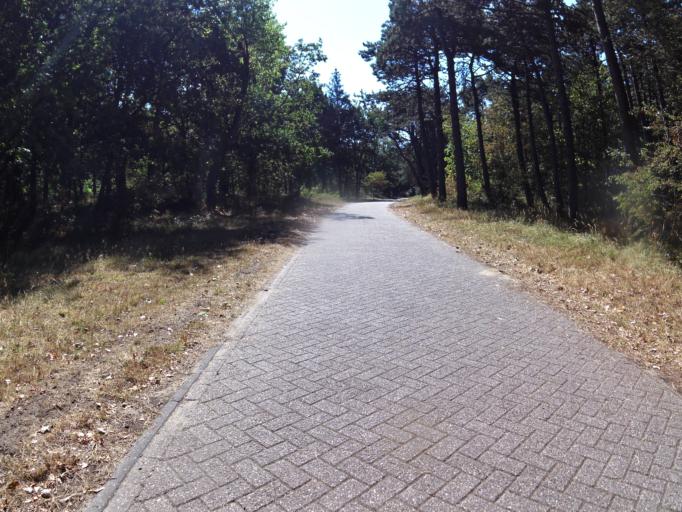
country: NL
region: North Holland
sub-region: Gemeente Beverwijk
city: Beverwijk
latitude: 52.5089
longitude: 4.6141
